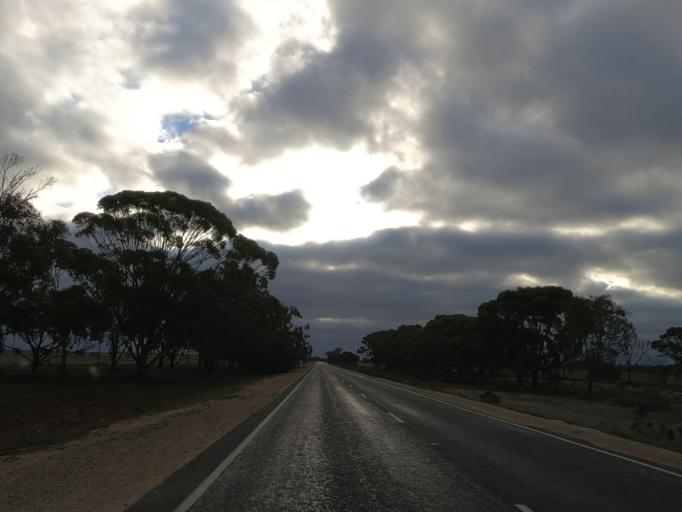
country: AU
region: Victoria
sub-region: Swan Hill
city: Swan Hill
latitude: -35.6571
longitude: 143.8526
